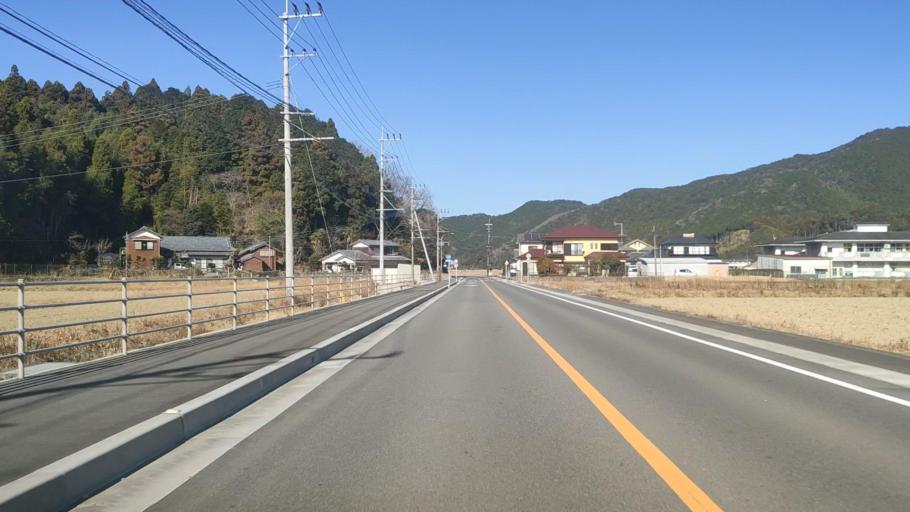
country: JP
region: Oita
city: Saiki
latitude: 32.9225
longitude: 131.9267
